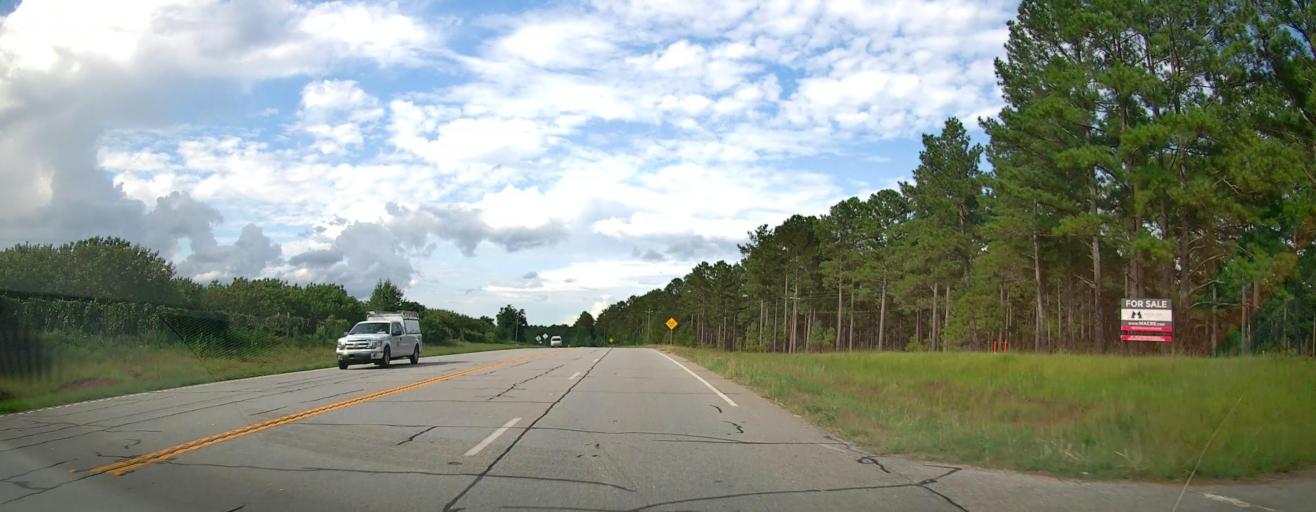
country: US
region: Georgia
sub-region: Meriwether County
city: Greenville
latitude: 33.0073
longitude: -84.5673
